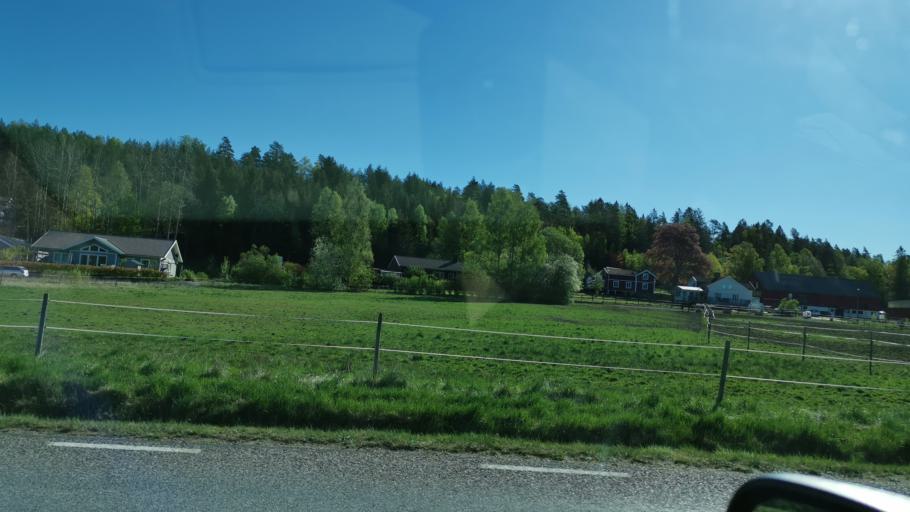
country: SE
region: Vaestra Goetaland
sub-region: Uddevalla Kommun
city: Uddevalla
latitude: 58.2928
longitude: 11.8985
